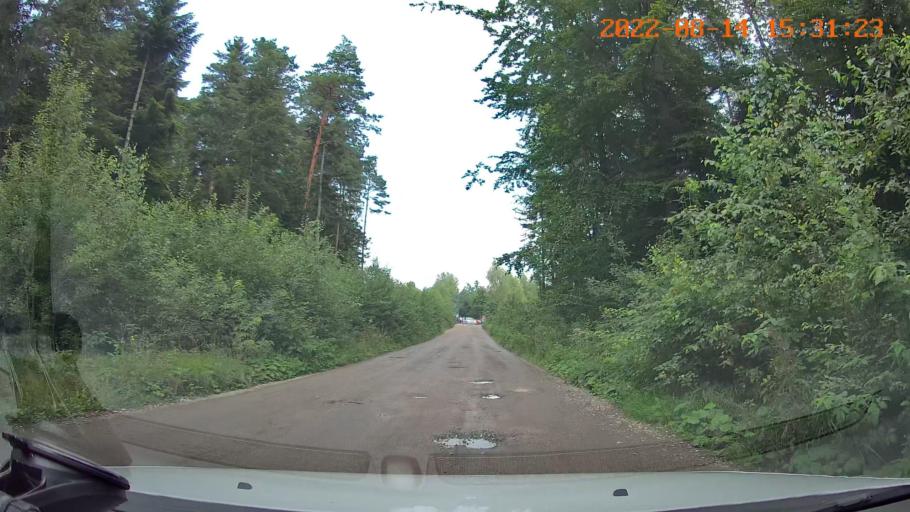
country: PL
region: Swietokrzyskie
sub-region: Powiat kielecki
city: Zagnansk
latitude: 50.9670
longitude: 20.6629
